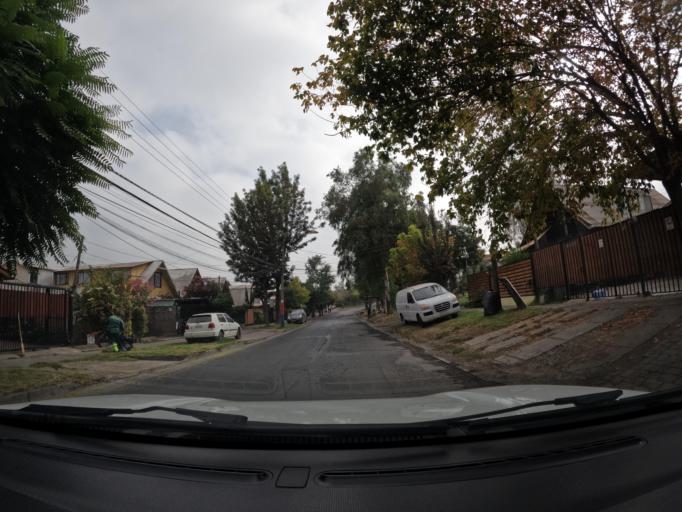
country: CL
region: Santiago Metropolitan
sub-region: Provincia de Santiago
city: Villa Presidente Frei, Nunoa, Santiago, Chile
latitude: -33.4704
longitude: -70.5355
